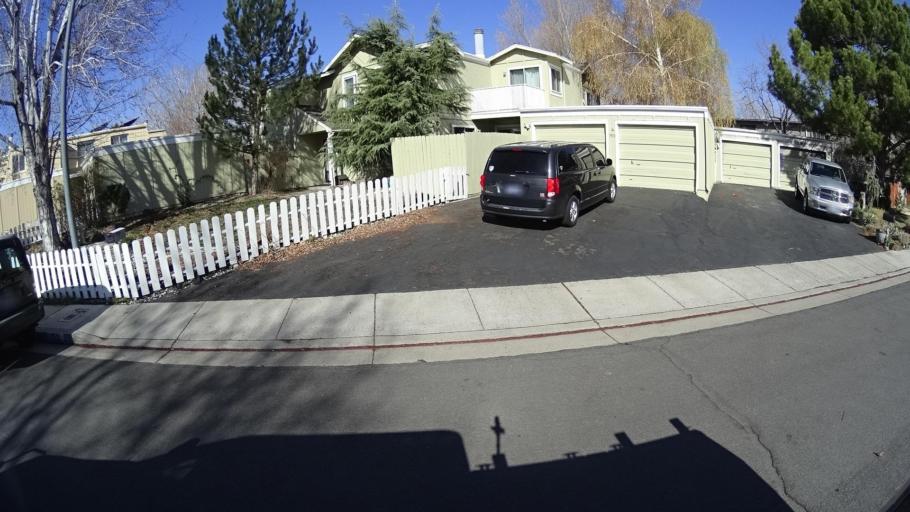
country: US
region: Nevada
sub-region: Washoe County
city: Sparks
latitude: 39.4567
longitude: -119.7704
